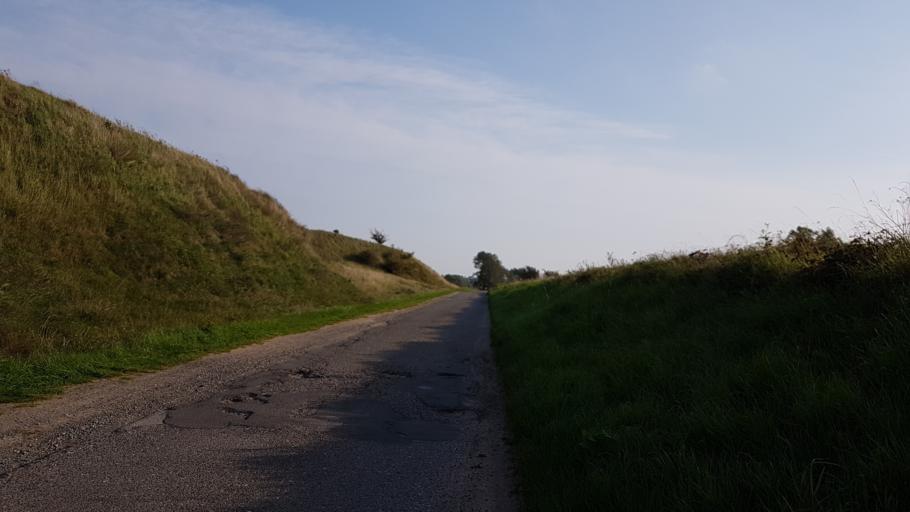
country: DE
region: Mecklenburg-Vorpommern
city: Sagard
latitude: 54.5368
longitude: 13.5106
